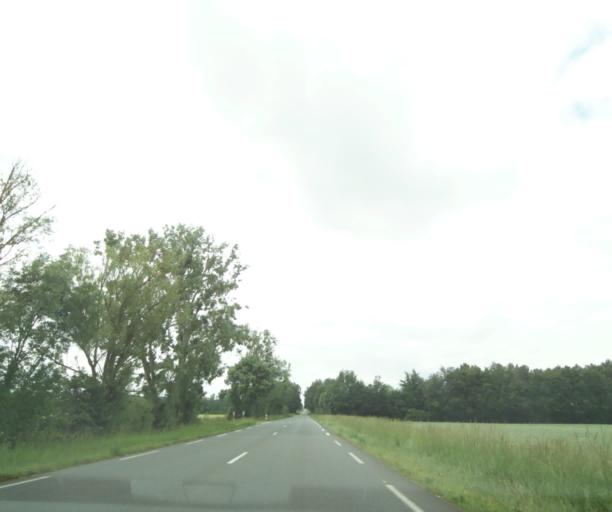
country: FR
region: Pays de la Loire
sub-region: Departement de Maine-et-Loire
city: Montreuil-Bellay
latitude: 47.1687
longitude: -0.1397
